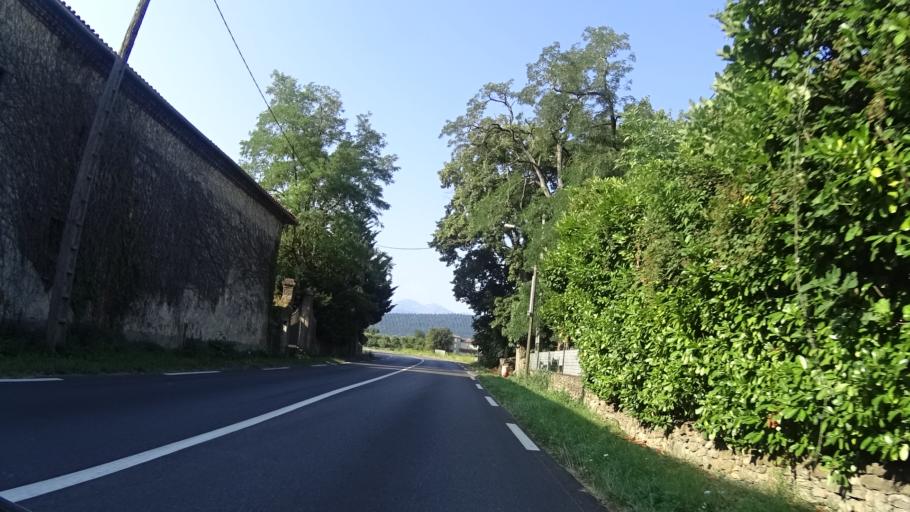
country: FR
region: Midi-Pyrenees
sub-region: Departement de l'Ariege
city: Lavelanet
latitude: 42.9811
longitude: 1.8695
